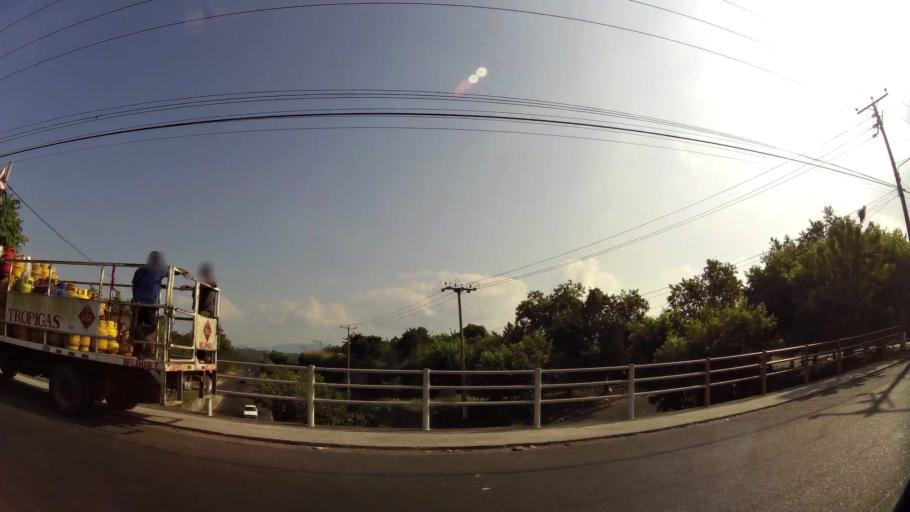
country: SV
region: San Salvador
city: Soyapango
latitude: 13.7162
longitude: -89.1290
